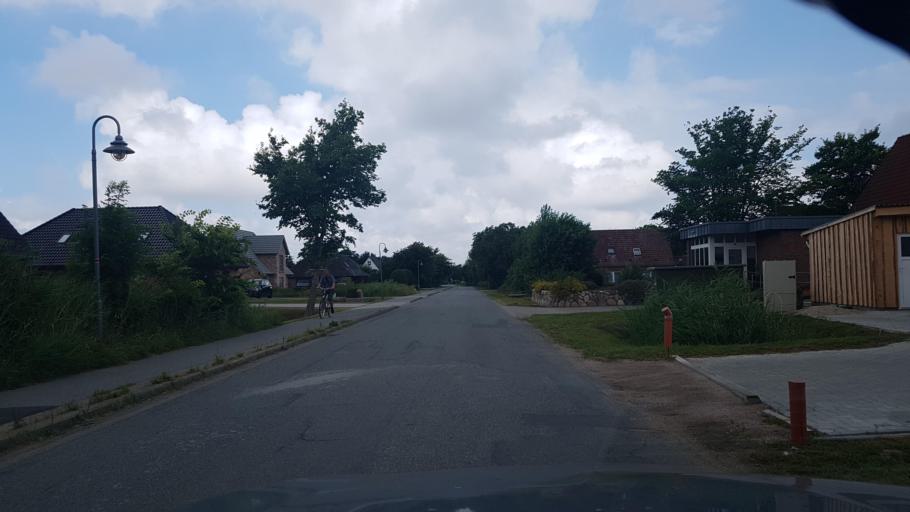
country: DE
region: Schleswig-Holstein
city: Elisabeth-Sophien-Koog
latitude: 54.4856
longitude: 8.8510
